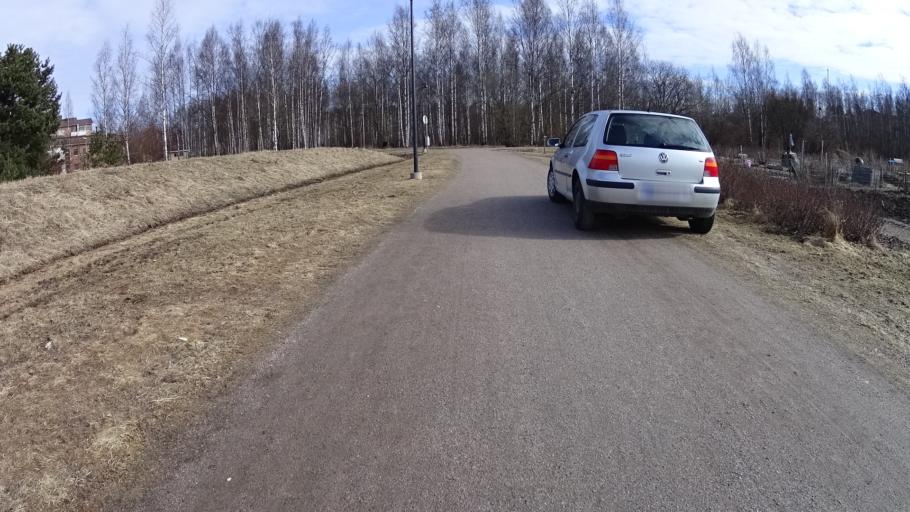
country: FI
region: Uusimaa
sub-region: Helsinki
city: Teekkarikylae
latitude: 60.2562
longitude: 24.8599
